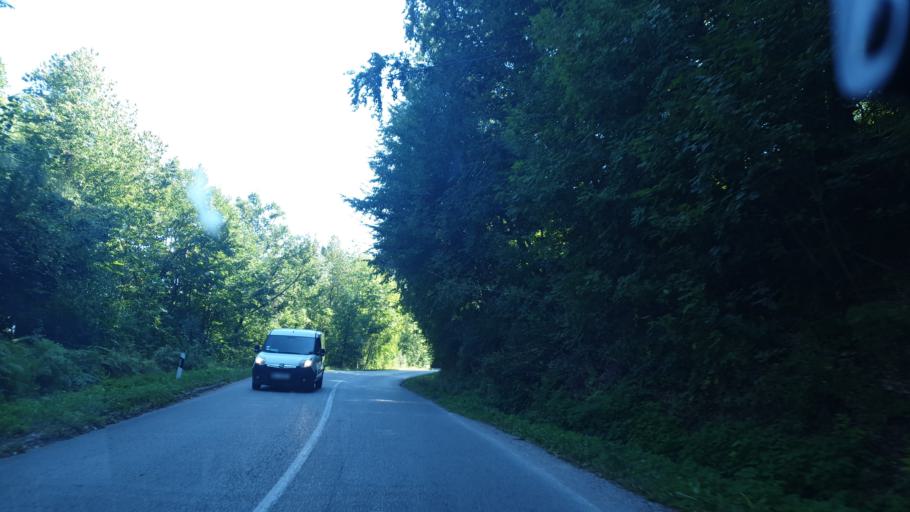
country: RS
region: Central Serbia
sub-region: Kolubarski Okrug
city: Mionica
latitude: 44.1561
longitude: 20.0058
